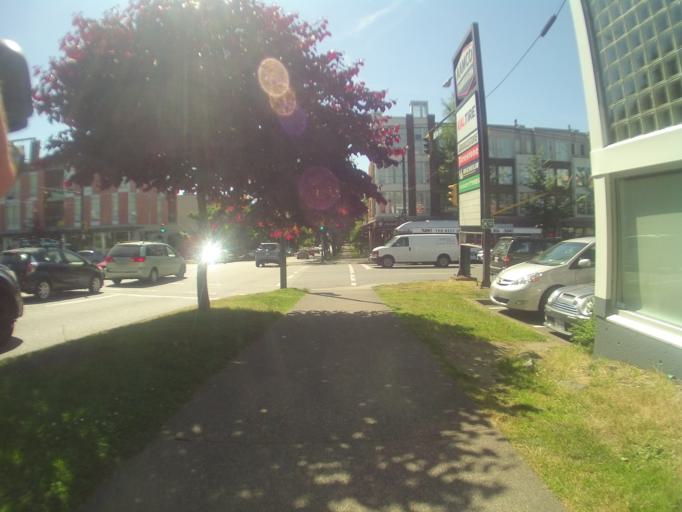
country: CA
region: British Columbia
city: West End
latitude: 49.2611
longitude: -123.1527
